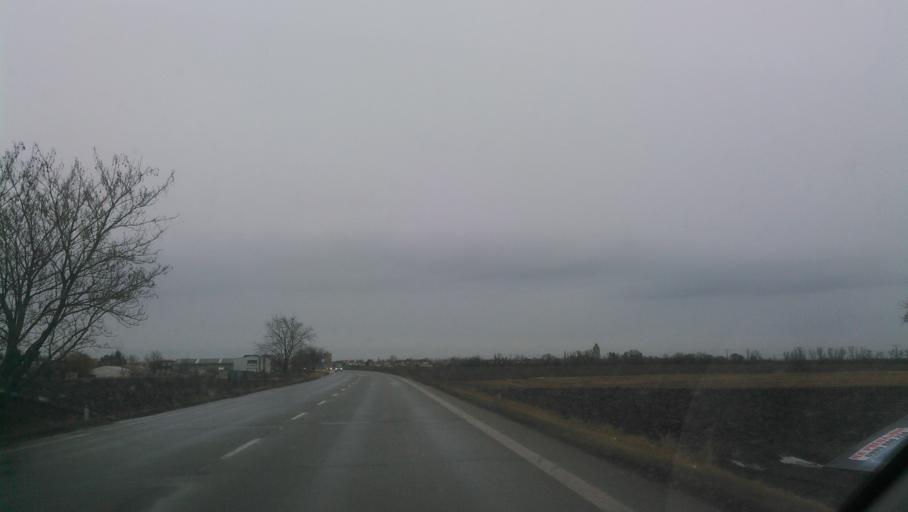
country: SK
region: Nitriansky
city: Sellye
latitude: 48.1628
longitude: 17.8436
